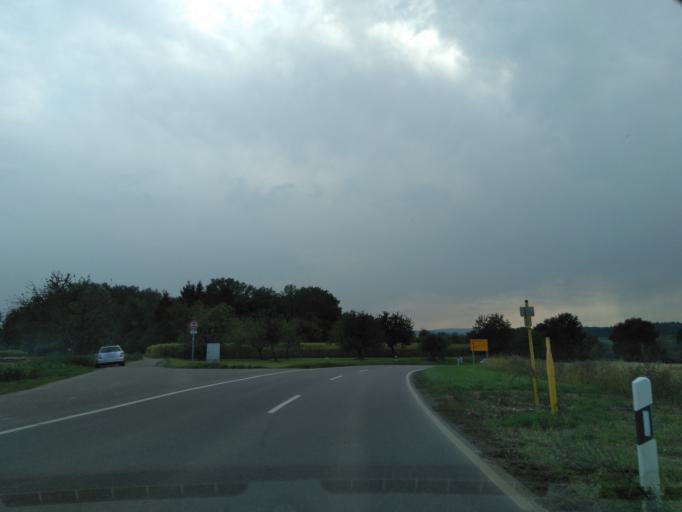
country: DE
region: Baden-Wuerttemberg
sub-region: Regierungsbezirk Stuttgart
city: Oberriexingen
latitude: 48.9473
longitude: 9.0547
